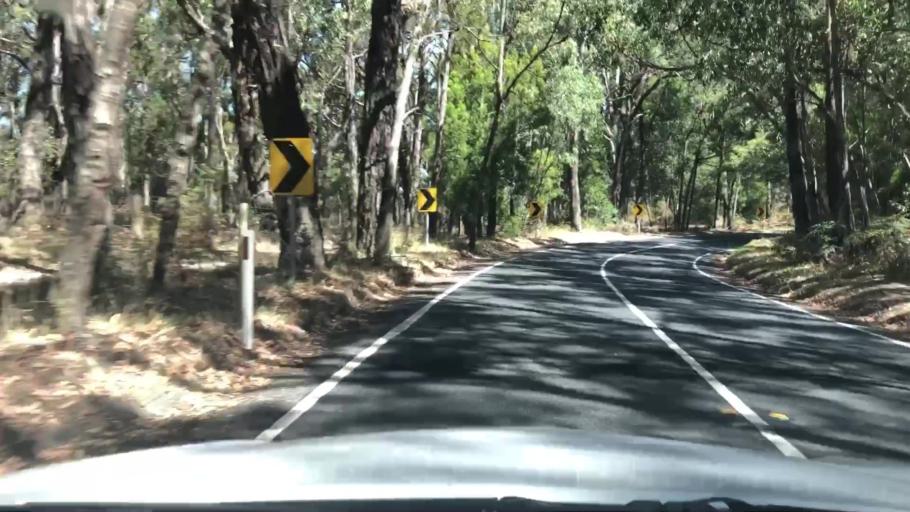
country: AU
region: Victoria
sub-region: Yarra Ranges
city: Macclesfield
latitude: -37.8367
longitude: 145.4888
